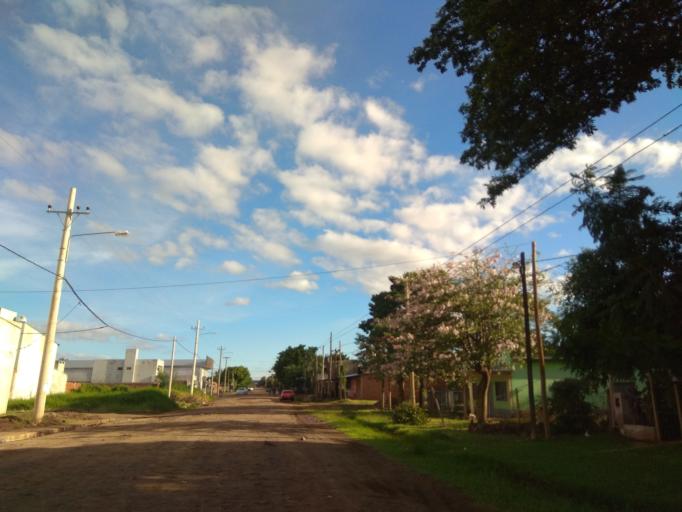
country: AR
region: Misiones
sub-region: Departamento de Capital
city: Posadas
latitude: -27.3834
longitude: -55.9263
